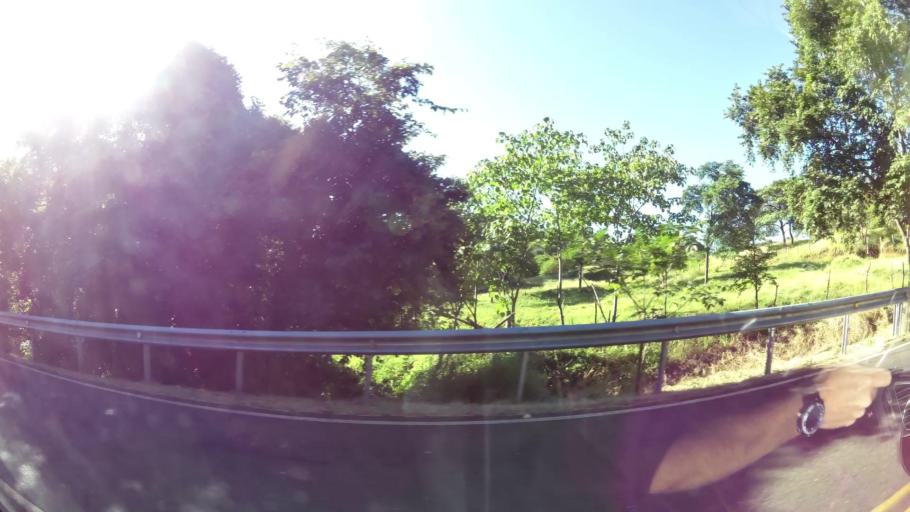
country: CR
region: Guanacaste
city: Belen
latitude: 10.3731
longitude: -85.6275
